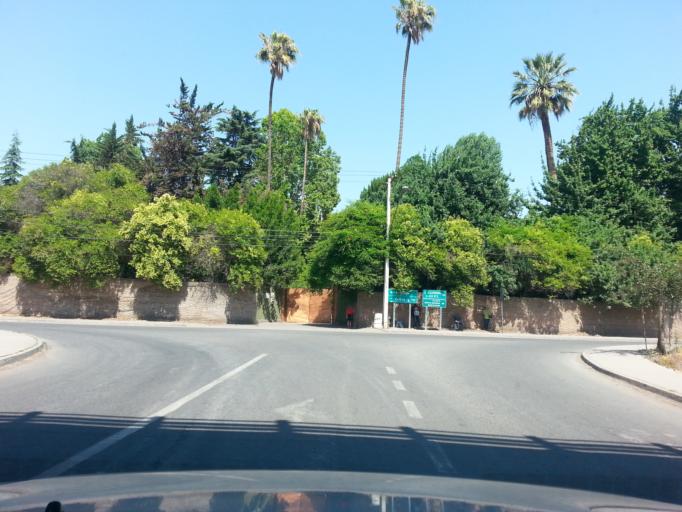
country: CL
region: Santiago Metropolitan
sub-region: Provincia de Chacabuco
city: Chicureo Abajo
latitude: -33.2854
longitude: -70.7017
